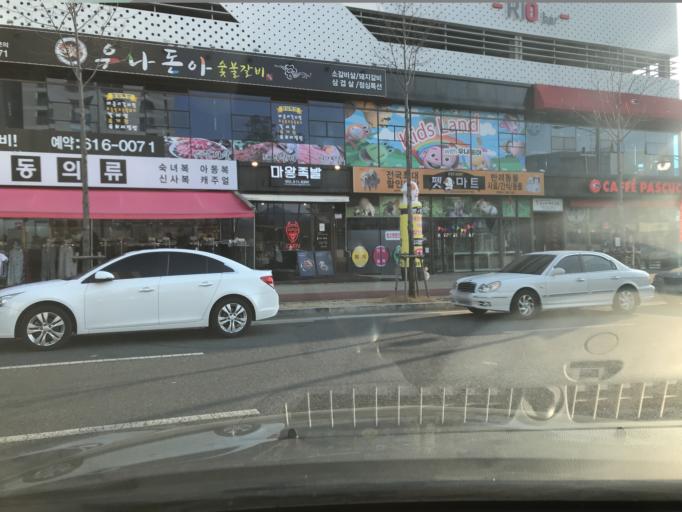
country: KR
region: Daegu
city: Hwawon
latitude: 35.6890
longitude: 128.4497
